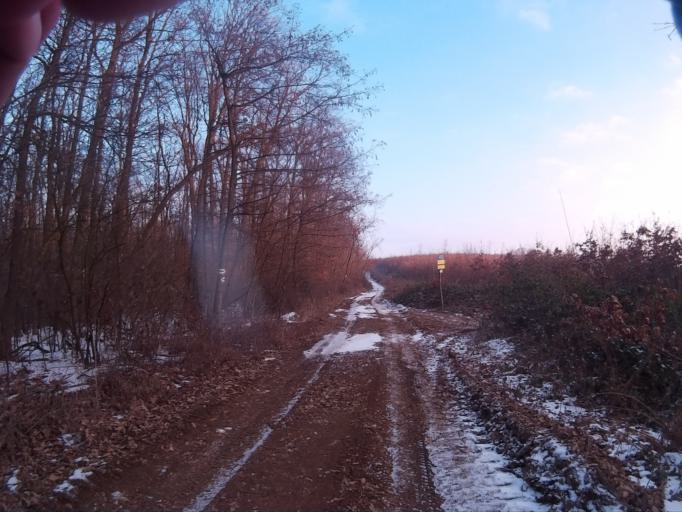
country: HU
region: Borsod-Abauj-Zemplen
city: Szendro
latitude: 48.4273
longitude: 20.8733
